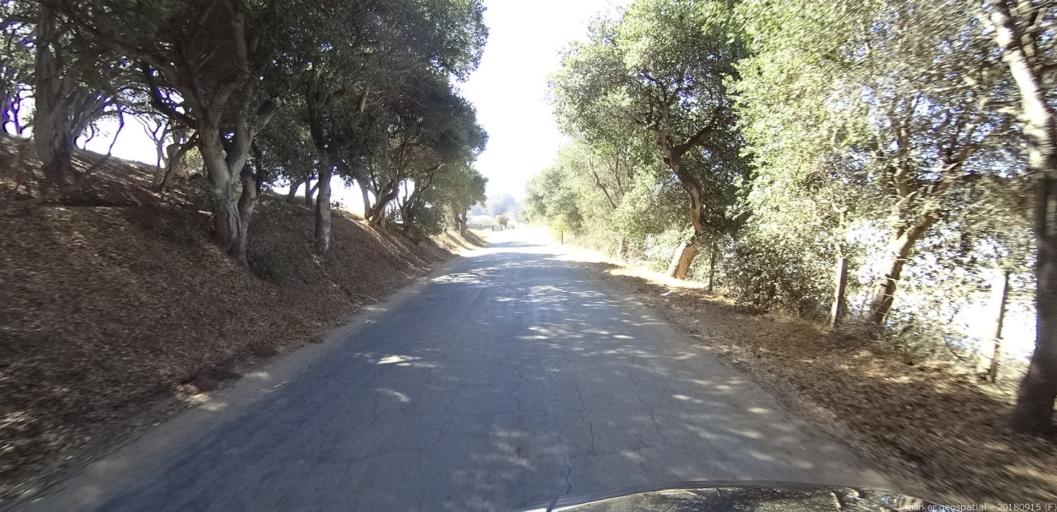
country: US
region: California
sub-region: Monterey County
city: Las Lomas
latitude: 36.8695
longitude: -121.7226
